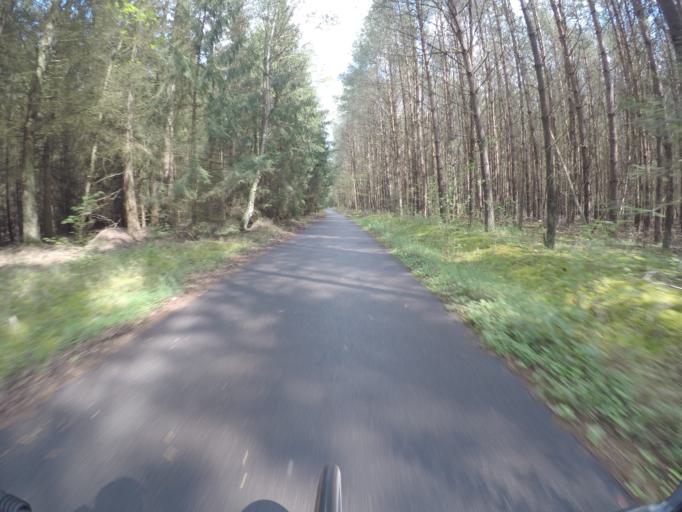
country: DE
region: Brandenburg
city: Marienwerder
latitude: 52.8687
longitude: 13.6155
